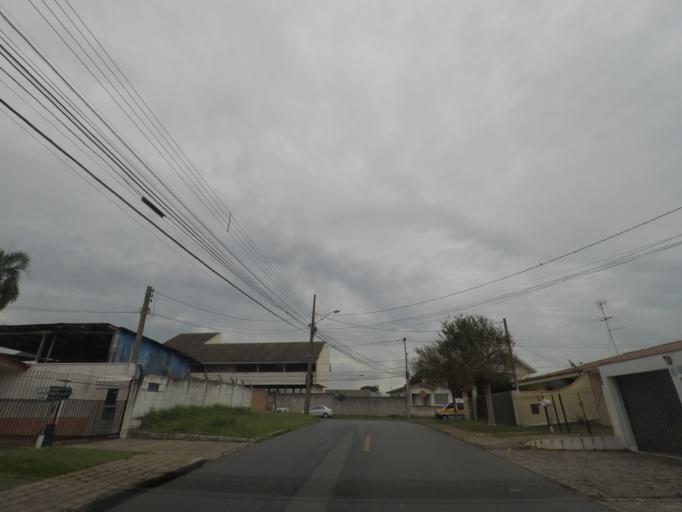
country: BR
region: Parana
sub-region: Curitiba
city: Curitiba
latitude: -25.4729
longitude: -49.3088
